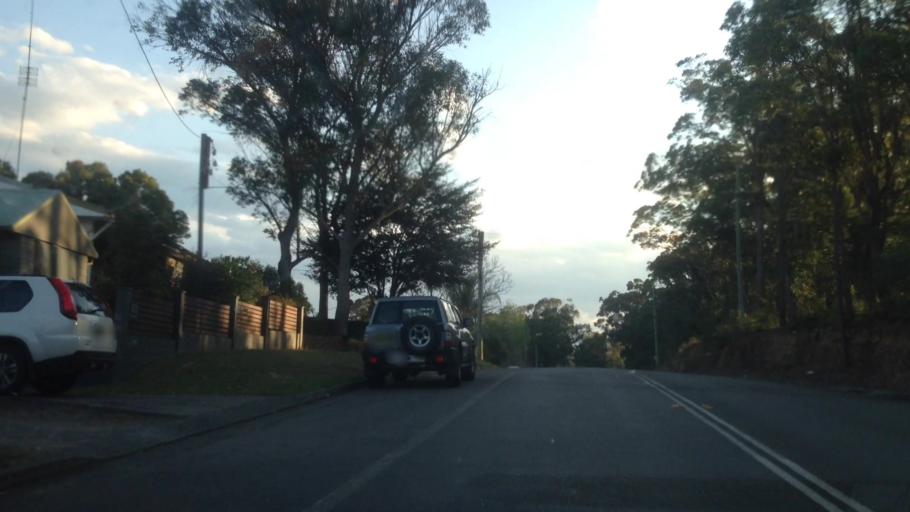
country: AU
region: New South Wales
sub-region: Lake Macquarie Shire
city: Cooranbong
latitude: -33.0642
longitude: 151.4701
